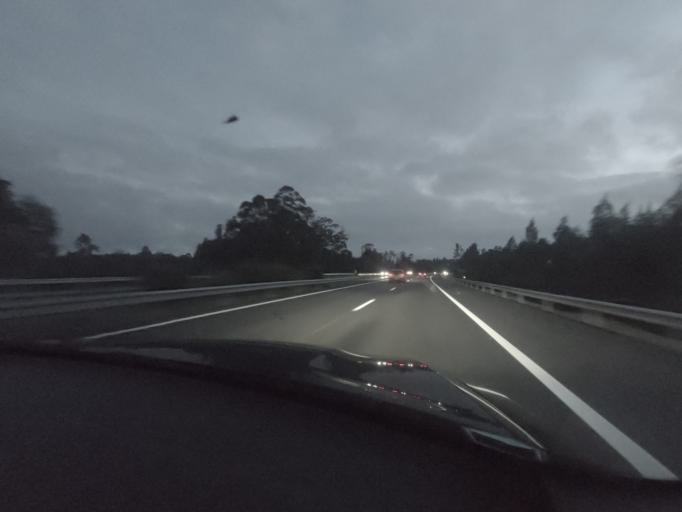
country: PT
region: Leiria
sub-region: Pombal
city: Pombal
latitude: 39.8943
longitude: -8.6896
